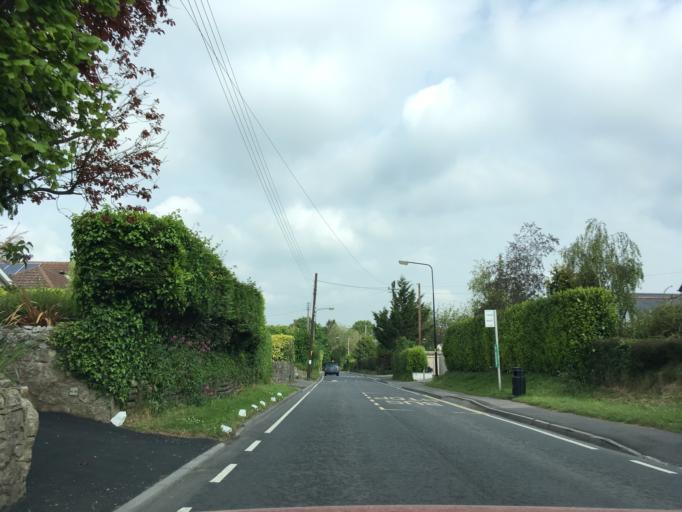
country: GB
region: England
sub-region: North Somerset
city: Nailsea
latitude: 51.4156
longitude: -2.7415
